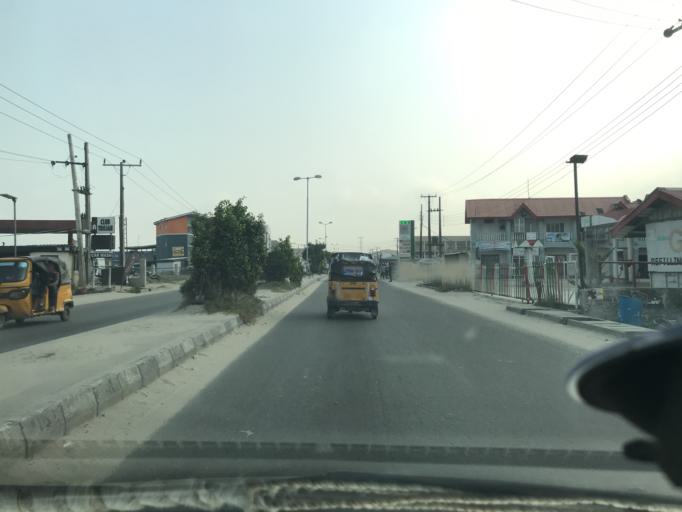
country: NG
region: Lagos
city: Ikoyi
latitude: 6.4855
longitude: 3.5759
